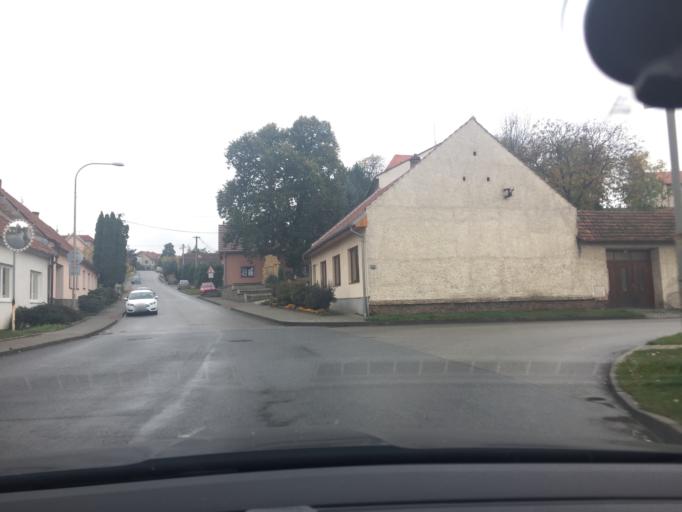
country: CZ
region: South Moravian
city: Blazovice
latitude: 49.1389
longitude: 16.7650
